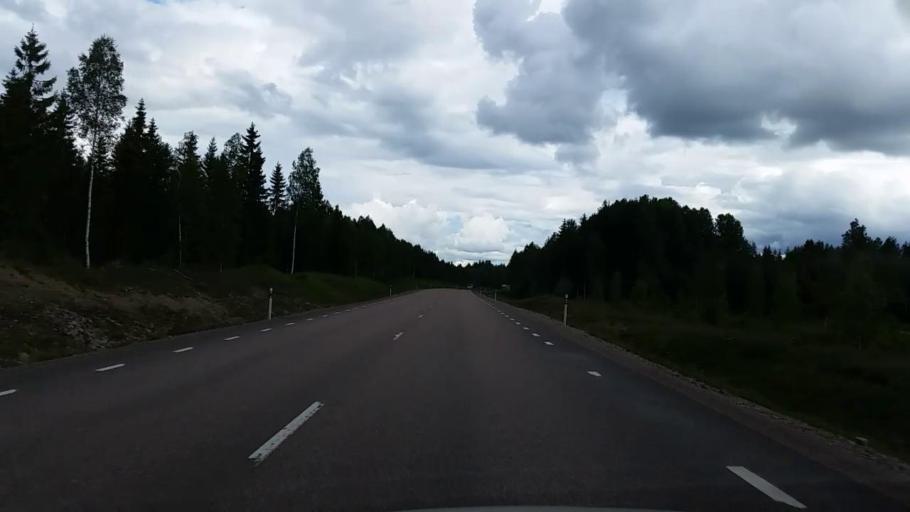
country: SE
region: Gaevleborg
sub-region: Hofors Kommun
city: Hofors
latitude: 60.4771
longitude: 16.4462
